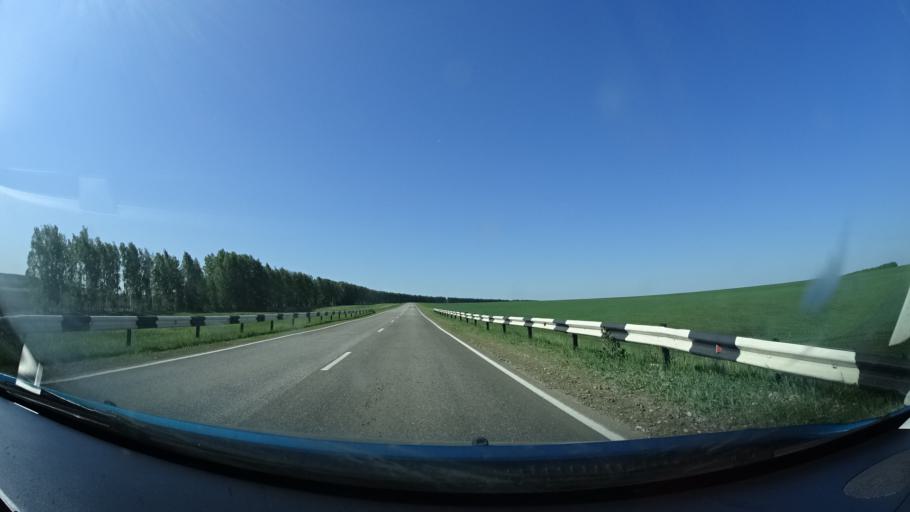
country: RU
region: Bashkortostan
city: Starobaltachevo
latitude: 55.9149
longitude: 55.7758
